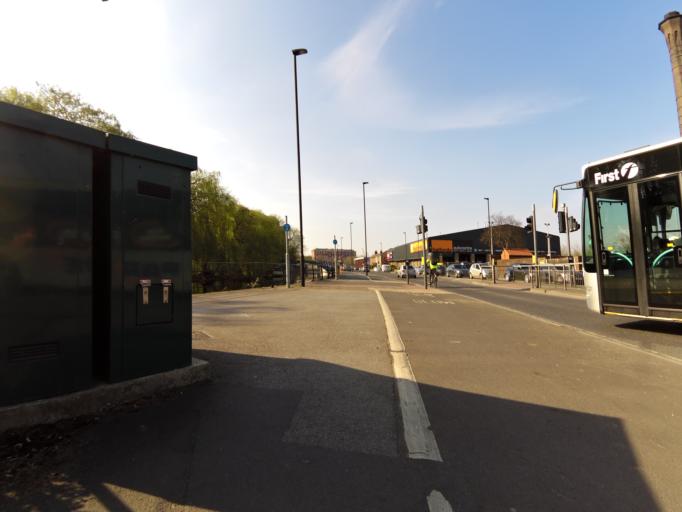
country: GB
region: England
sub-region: City of York
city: York
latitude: 53.9595
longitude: -1.0719
